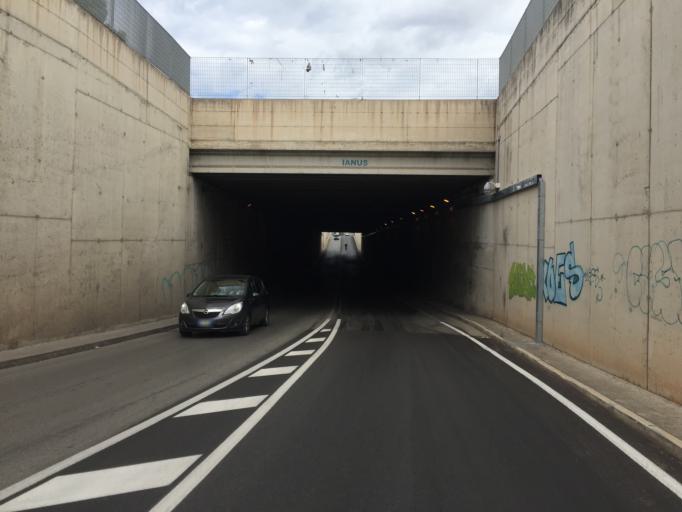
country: IT
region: Apulia
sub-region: Provincia di Bari
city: Bari
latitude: 41.1031
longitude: 16.8494
